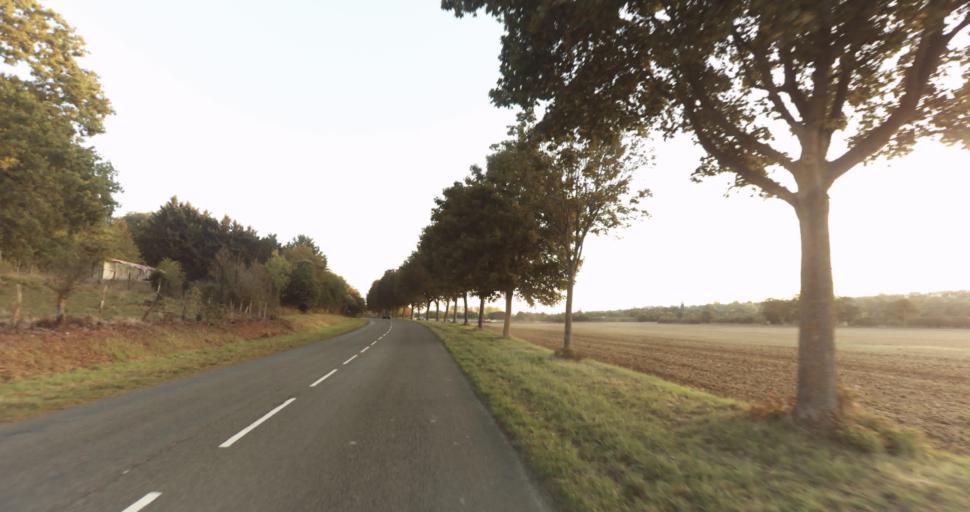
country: FR
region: Centre
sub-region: Departement d'Eure-et-Loir
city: Garnay
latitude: 48.7141
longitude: 1.3444
